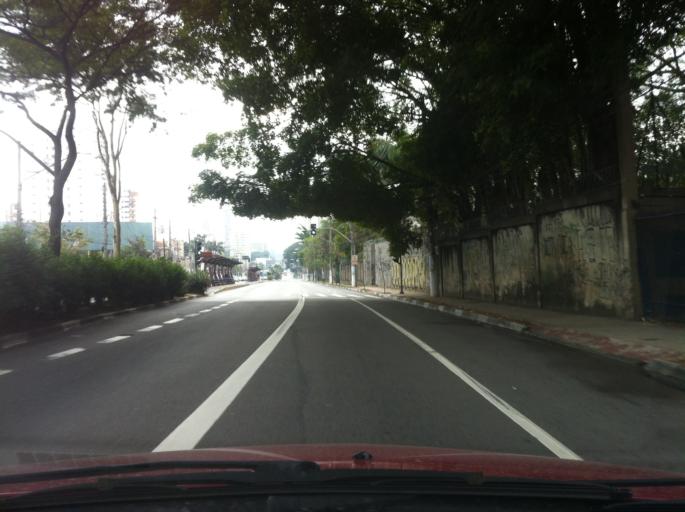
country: BR
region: Sao Paulo
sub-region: Diadema
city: Diadema
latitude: -23.6311
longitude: -46.6907
